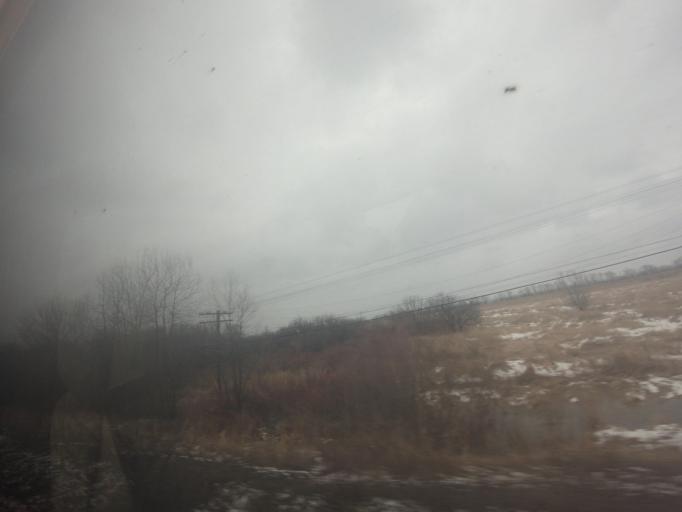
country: CA
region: Ontario
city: Cobourg
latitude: 43.9551
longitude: -78.2257
